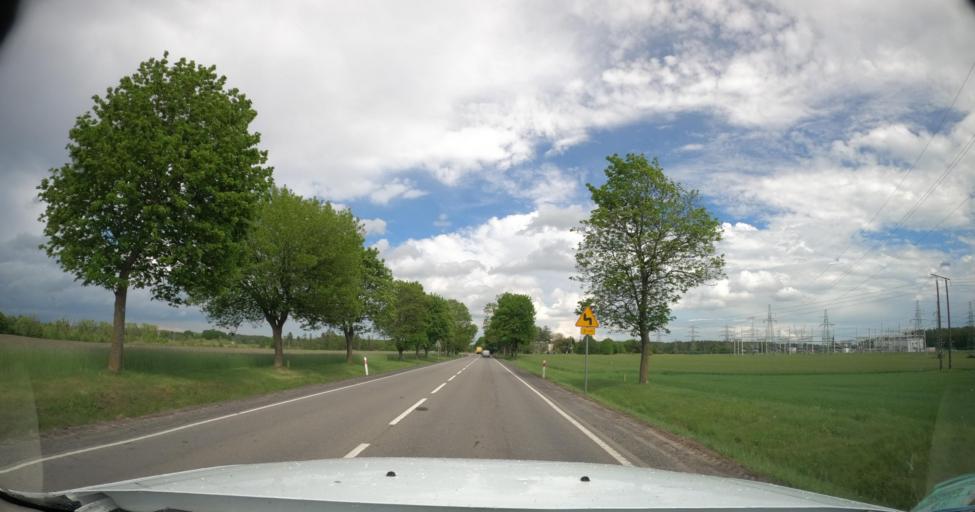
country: PL
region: Pomeranian Voivodeship
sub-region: Powiat kartuski
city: Banino
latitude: 54.3399
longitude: 18.4374
